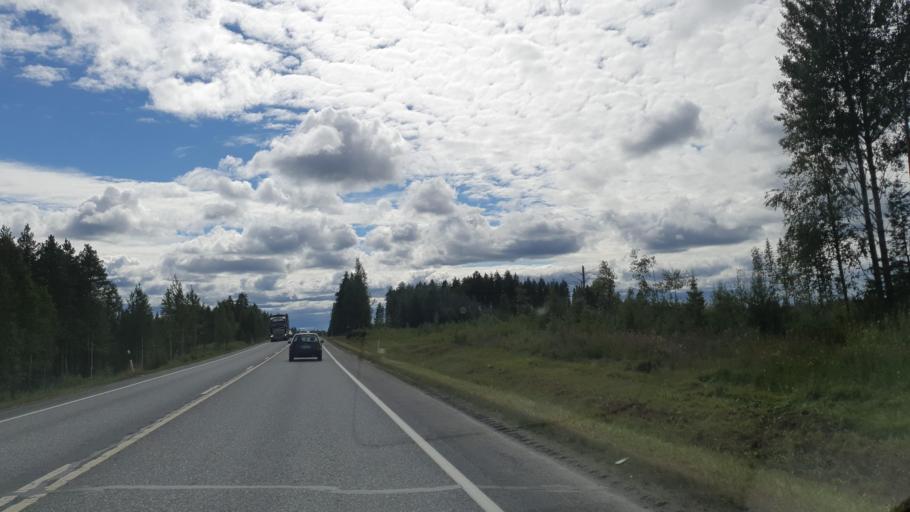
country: FI
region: Kainuu
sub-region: Kajaani
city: Kajaani
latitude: 64.1577
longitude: 27.5192
